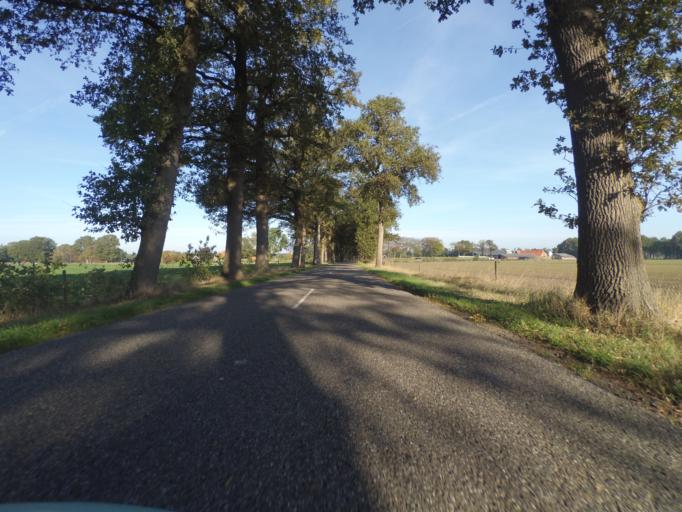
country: NL
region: Gelderland
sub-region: Berkelland
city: Eibergen
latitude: 52.0895
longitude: 6.6638
